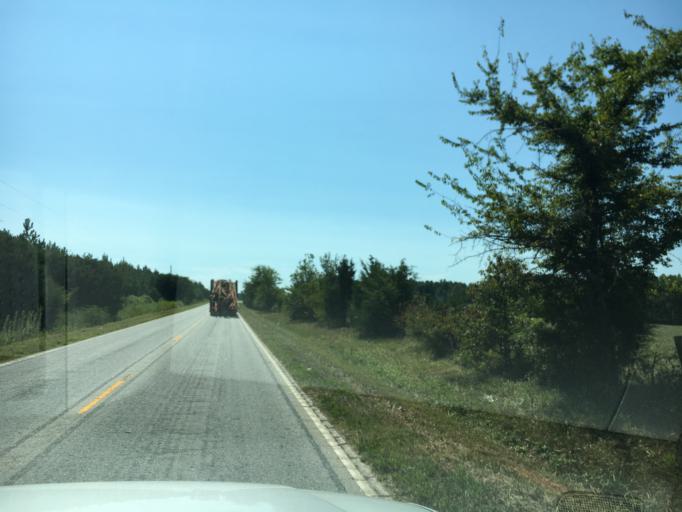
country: US
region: South Carolina
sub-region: Laurens County
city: Joanna
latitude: 34.4003
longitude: -81.8540
